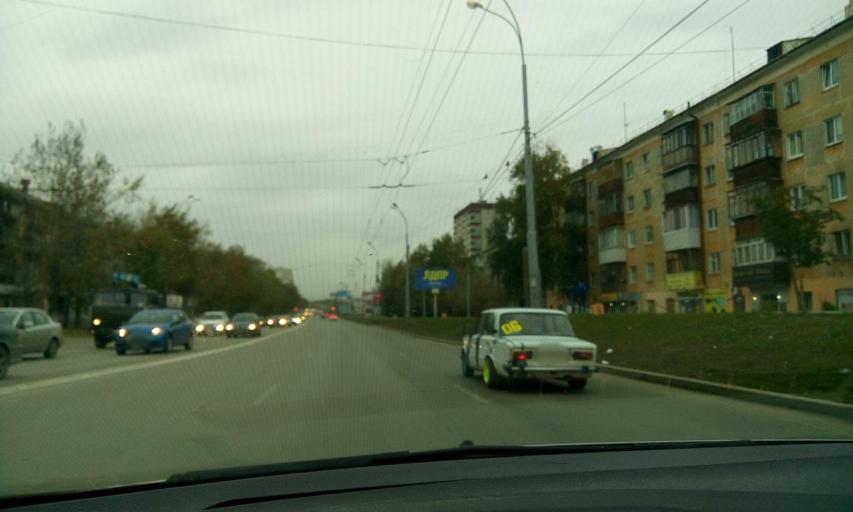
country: RU
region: Sverdlovsk
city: Yekaterinburg
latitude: 56.9072
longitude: 60.6135
